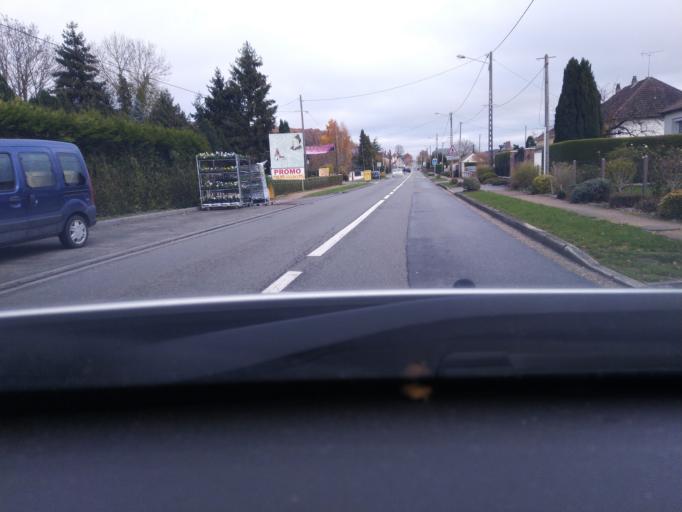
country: FR
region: Haute-Normandie
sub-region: Departement de la Seine-Maritime
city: Duclair
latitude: 49.4702
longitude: 0.8589
